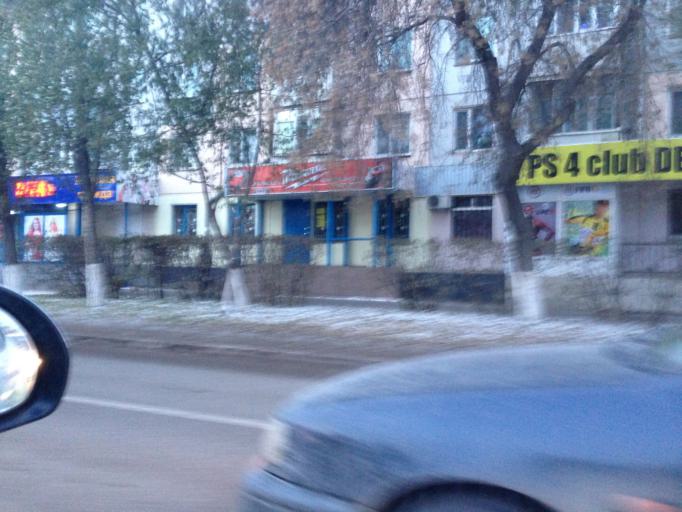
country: KZ
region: Astana Qalasy
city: Astana
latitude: 51.1822
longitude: 71.4092
